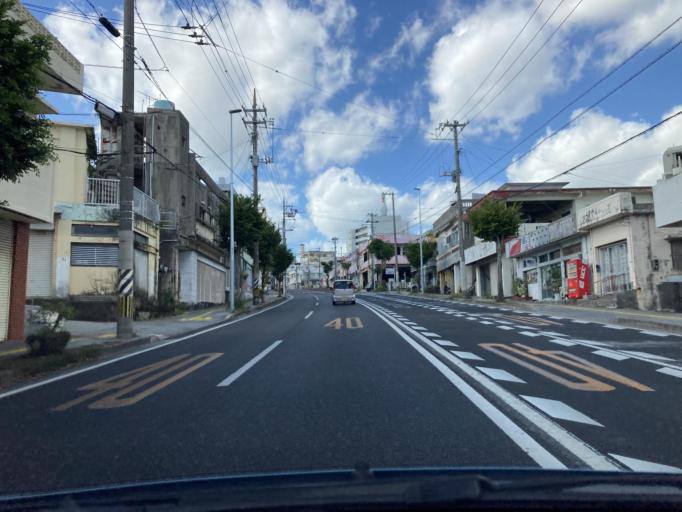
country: JP
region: Okinawa
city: Okinawa
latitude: 26.3376
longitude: 127.8057
